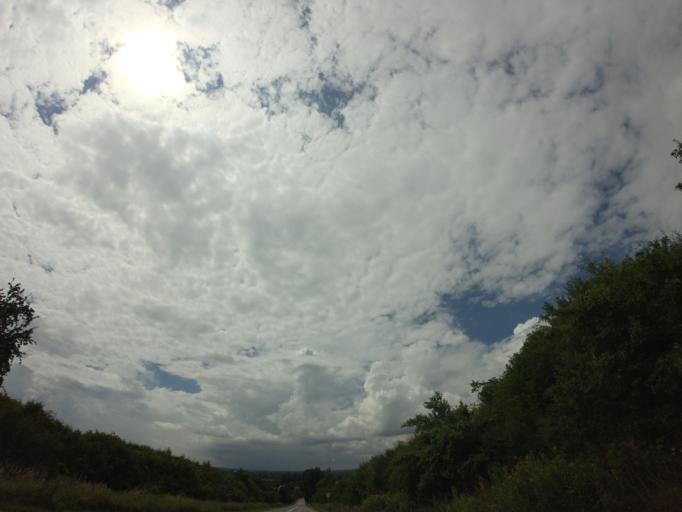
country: PL
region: Lublin Voivodeship
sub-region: Powiat opolski
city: Wilkow
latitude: 51.2699
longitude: 21.9122
